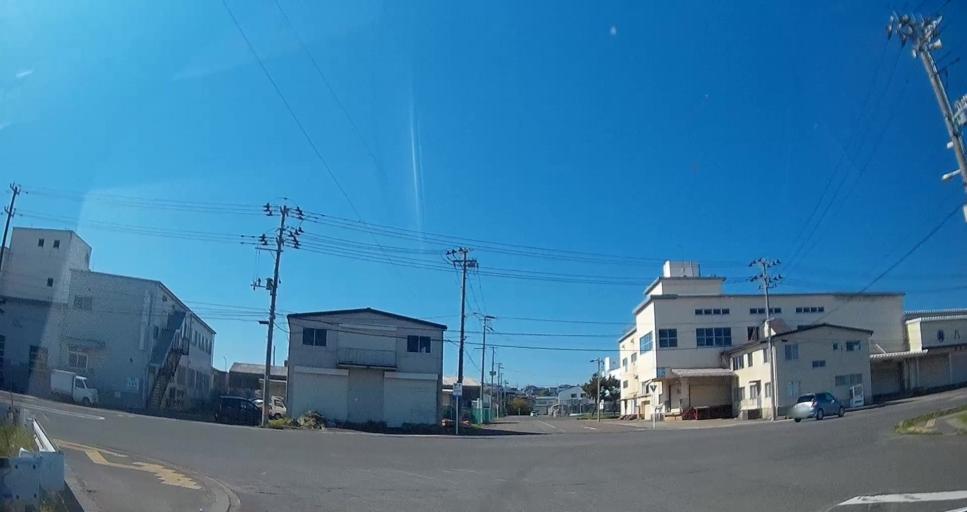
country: JP
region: Aomori
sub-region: Hachinohe Shi
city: Uchimaru
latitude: 40.5268
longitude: 141.5348
